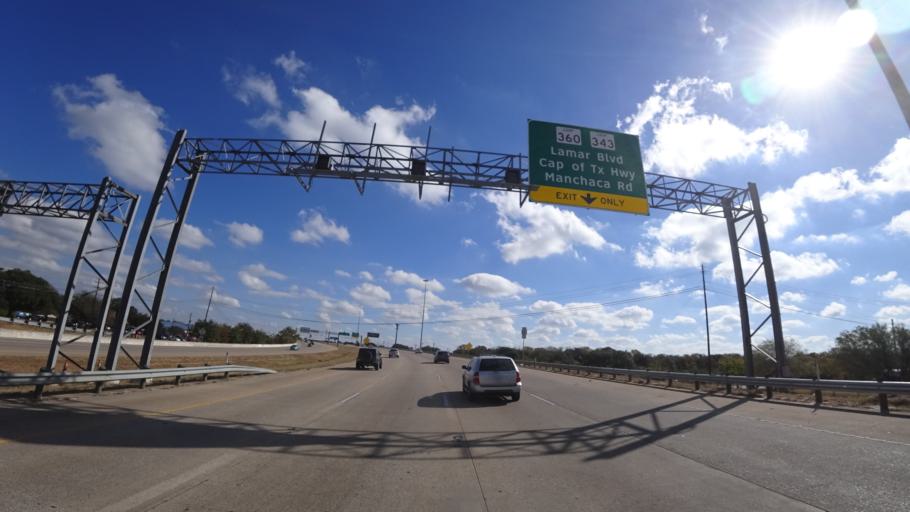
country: US
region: Texas
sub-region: Travis County
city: Rollingwood
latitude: 30.2318
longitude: -97.8064
